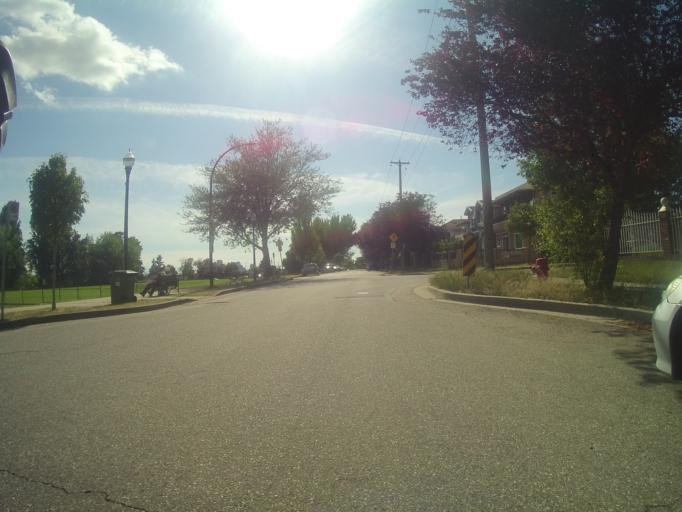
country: CA
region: British Columbia
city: Vancouver
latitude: 49.2165
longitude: -123.0852
